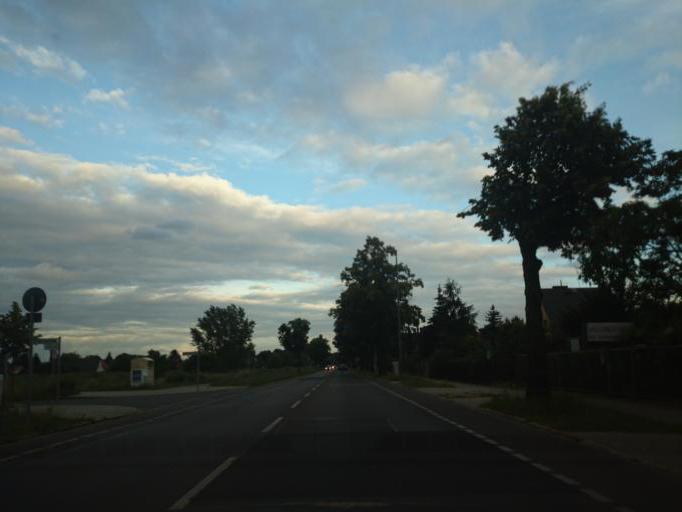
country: DE
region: Berlin
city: Biesdorf
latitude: 52.5004
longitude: 13.5620
